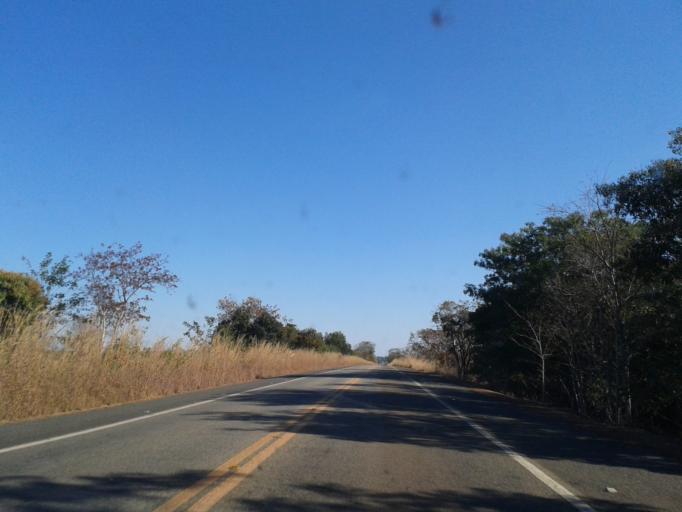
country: BR
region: Goias
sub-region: Mozarlandia
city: Mozarlandia
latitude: -15.0490
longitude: -50.6087
